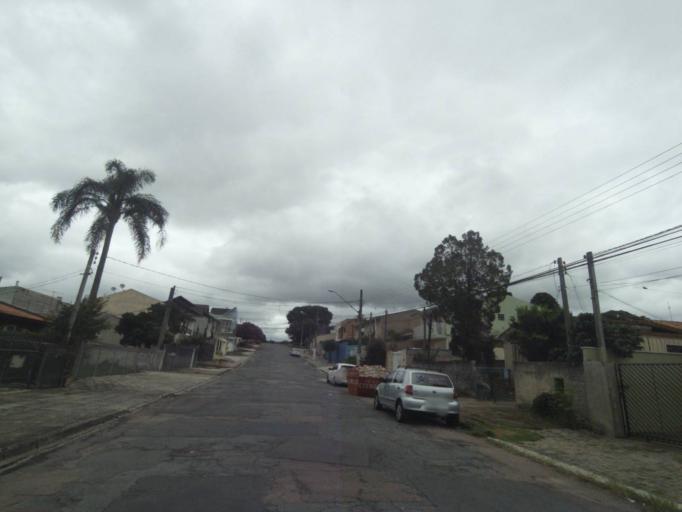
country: BR
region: Parana
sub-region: Curitiba
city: Curitiba
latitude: -25.4824
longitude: -49.2865
